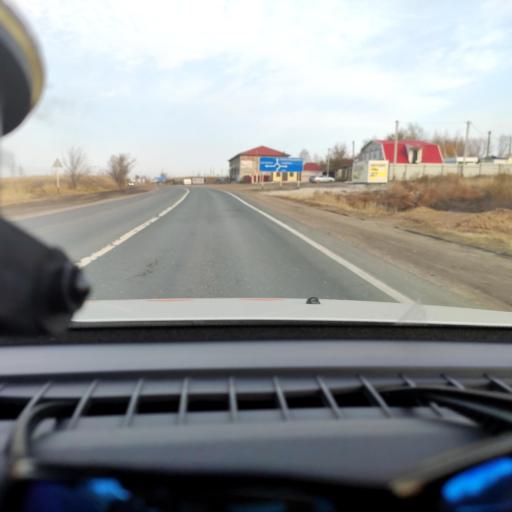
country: RU
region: Samara
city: Chapayevsk
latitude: 52.9937
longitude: 49.7677
